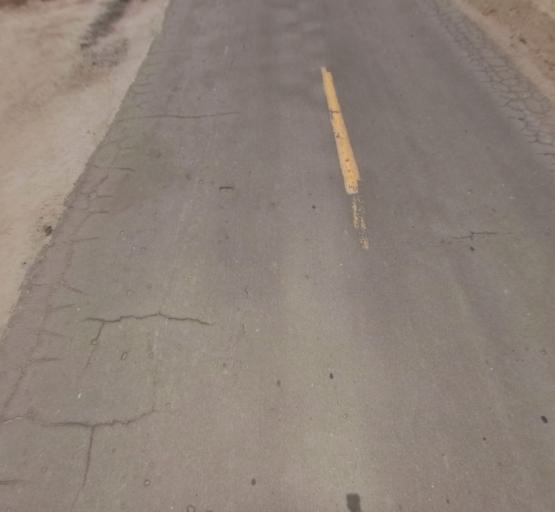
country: US
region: California
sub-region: Madera County
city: Madera
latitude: 36.9093
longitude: -120.1538
